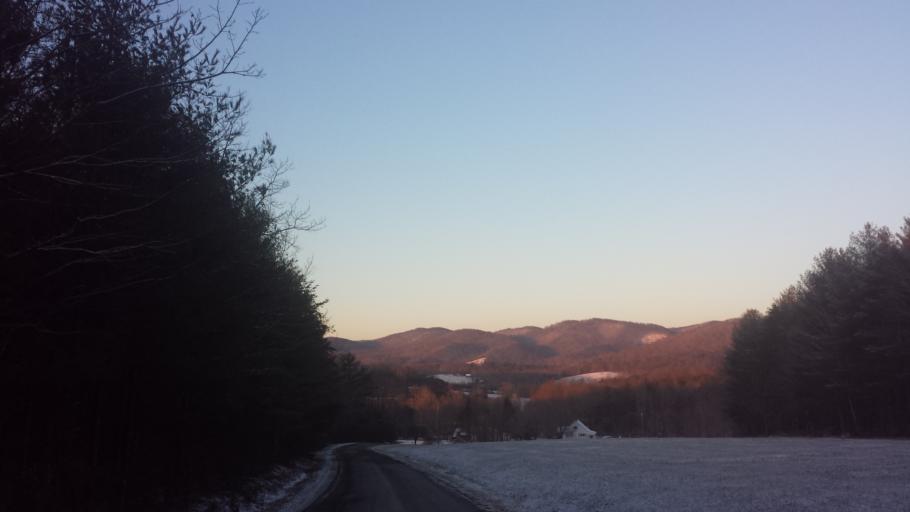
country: US
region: Virginia
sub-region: Franklin County
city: Ferrum
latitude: 36.9567
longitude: -79.9511
